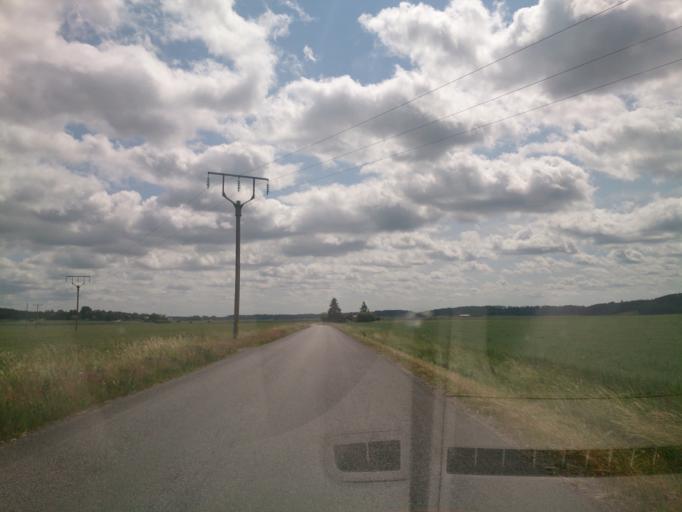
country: SE
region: OEstergoetland
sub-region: Norrkopings Kommun
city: Krokek
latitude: 58.5257
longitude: 16.4808
